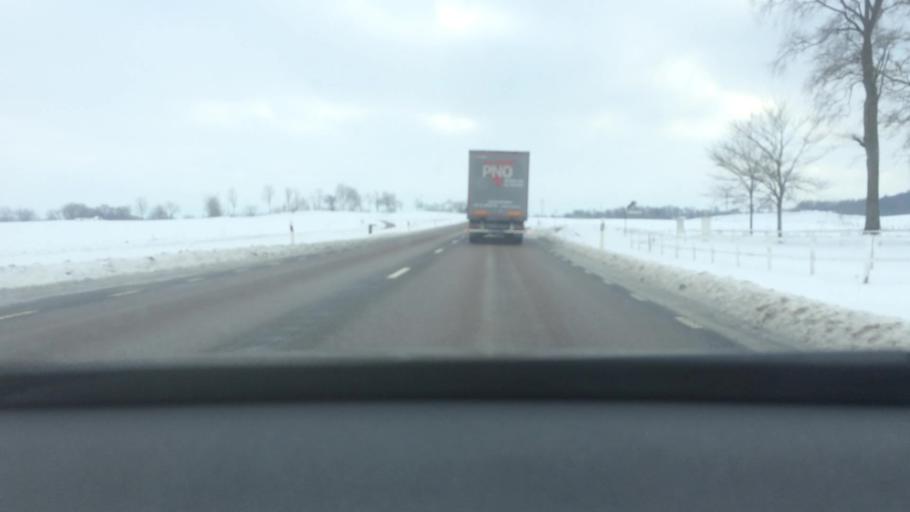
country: SE
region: Vaestra Goetaland
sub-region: Falkopings Kommun
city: Falkoeping
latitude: 58.2031
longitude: 13.5606
